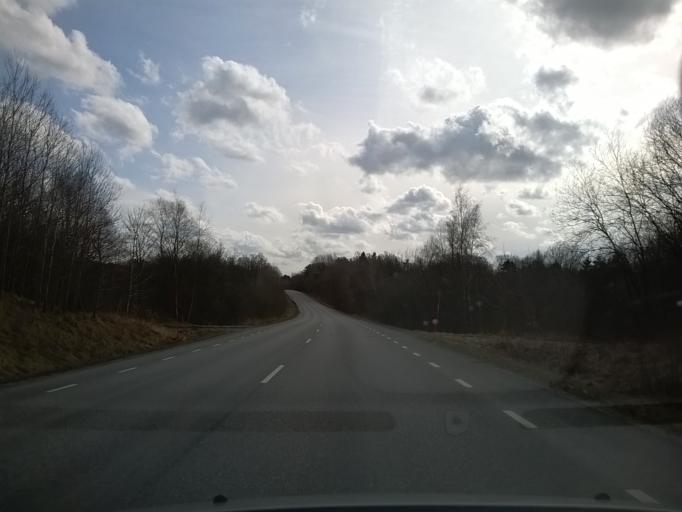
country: SE
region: Vaestra Goetaland
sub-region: Kungalvs Kommun
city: Kode
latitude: 57.9561
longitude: 11.8470
